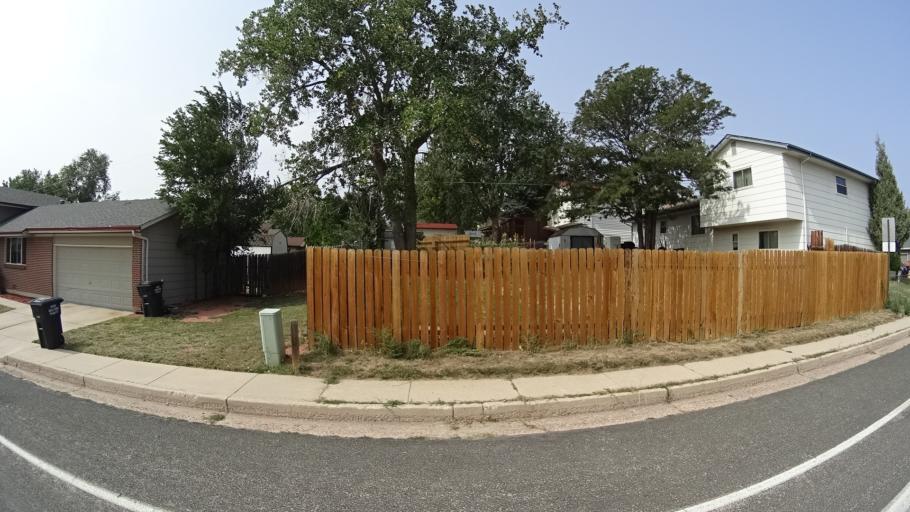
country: US
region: Colorado
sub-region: El Paso County
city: Stratmoor
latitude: 38.7986
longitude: -104.7678
